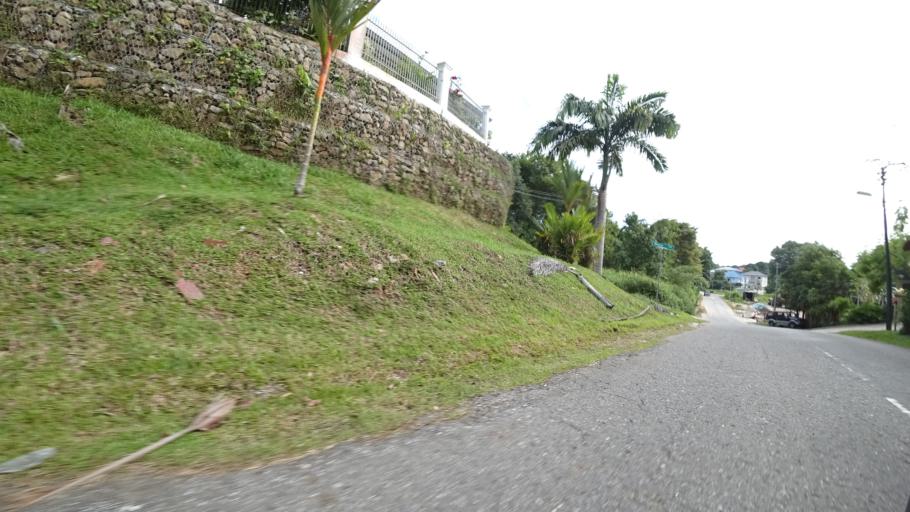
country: BN
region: Brunei and Muara
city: Bandar Seri Begawan
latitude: 4.8924
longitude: 114.9270
